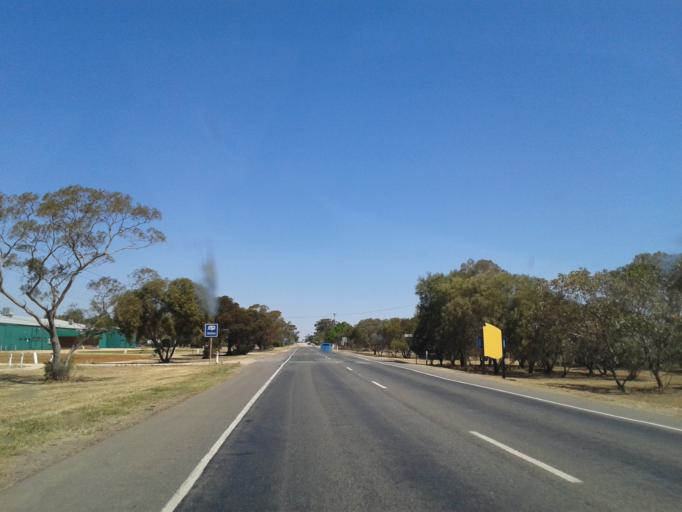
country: AU
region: Victoria
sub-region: Swan Hill
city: Swan Hill
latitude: -35.1791
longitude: 143.3772
